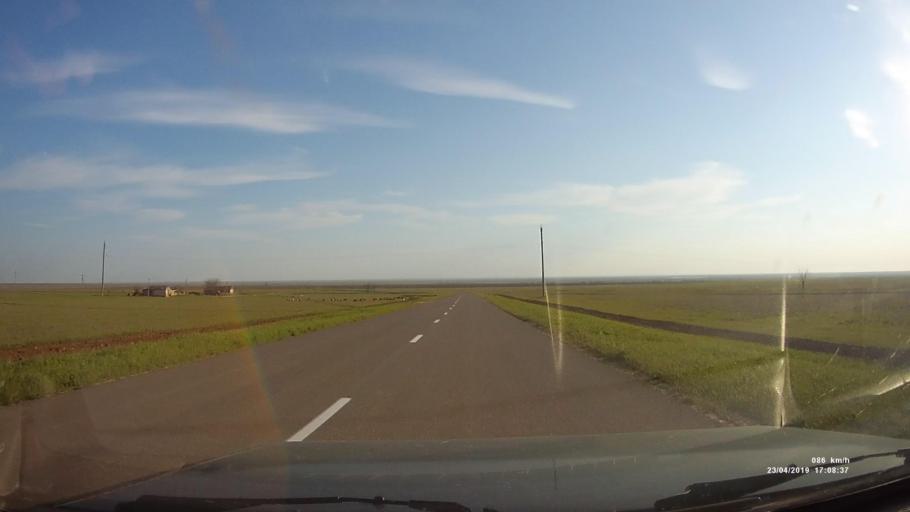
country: RU
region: Kalmykiya
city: Priyutnoye
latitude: 46.2690
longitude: 43.4862
